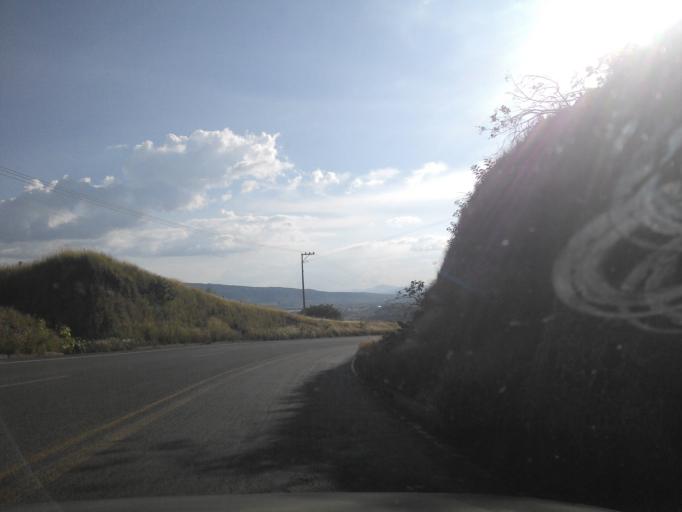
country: MX
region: Jalisco
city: Atotonilco el Alto
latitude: 20.5552
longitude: -102.5145
